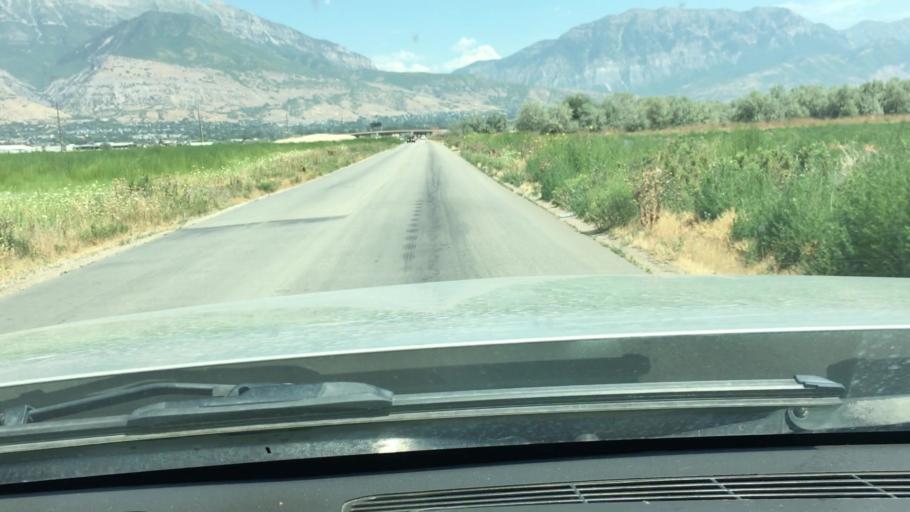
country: US
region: Utah
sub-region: Utah County
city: Pleasant Grove
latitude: 40.3441
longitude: -111.7715
